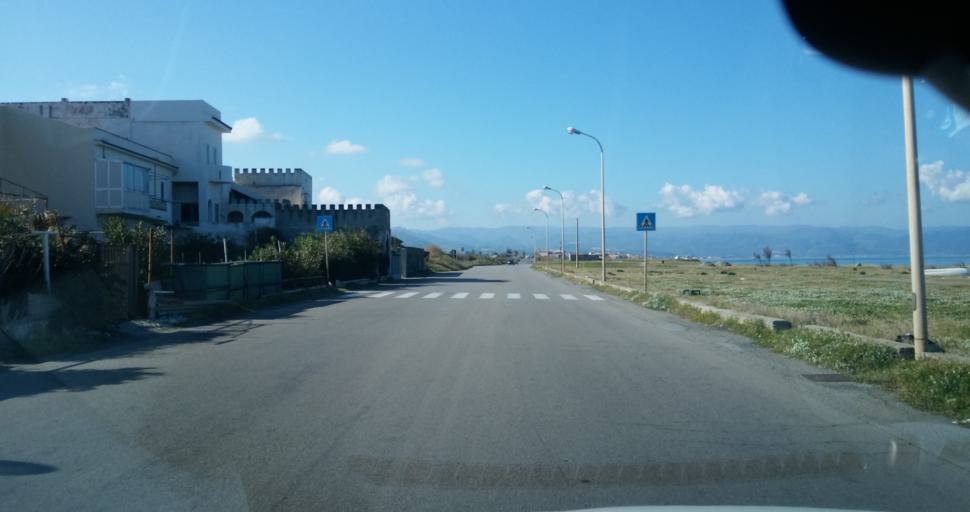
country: IT
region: Sicily
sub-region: Messina
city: Barcellona Pozzo di Gotto
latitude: 38.1867
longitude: 15.2140
